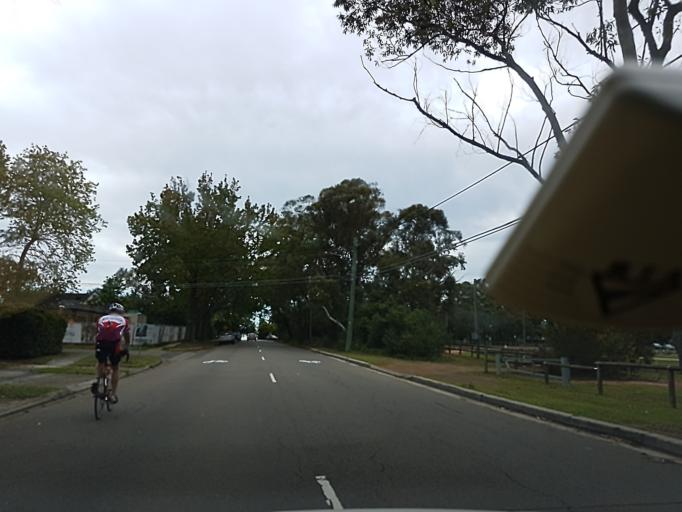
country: AU
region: New South Wales
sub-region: Warringah
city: Davidson
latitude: -33.7405
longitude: 151.2163
